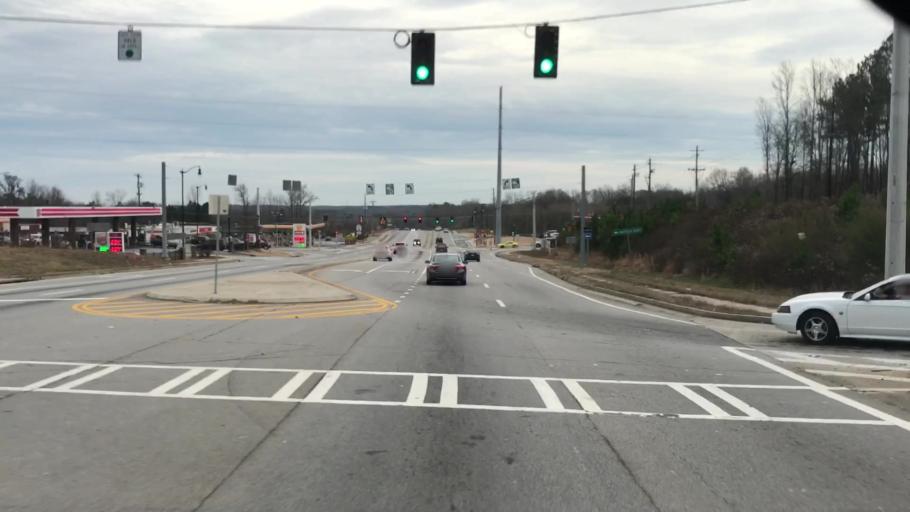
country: US
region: Georgia
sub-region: Jackson County
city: Hoschton
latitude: 34.0954
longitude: -83.8109
